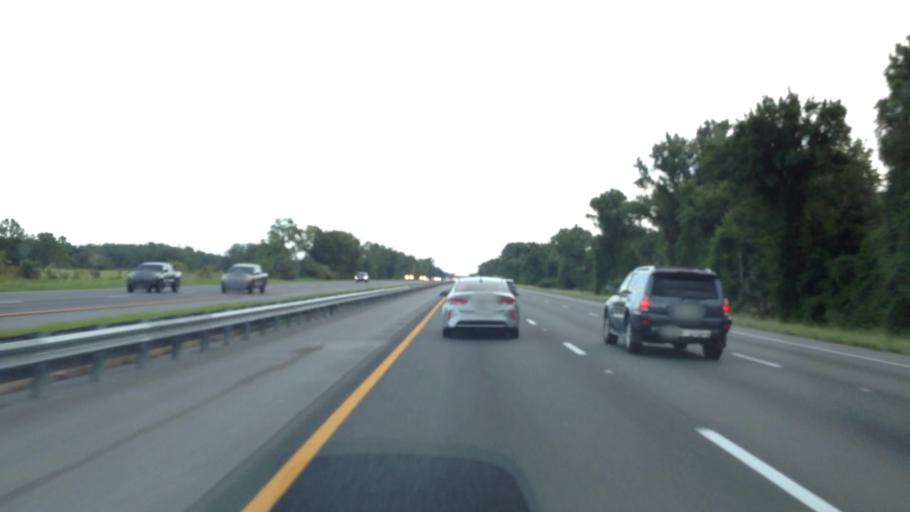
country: US
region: Florida
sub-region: Sumter County
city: Lake Panasoffkee
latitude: 28.8188
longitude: -82.0893
